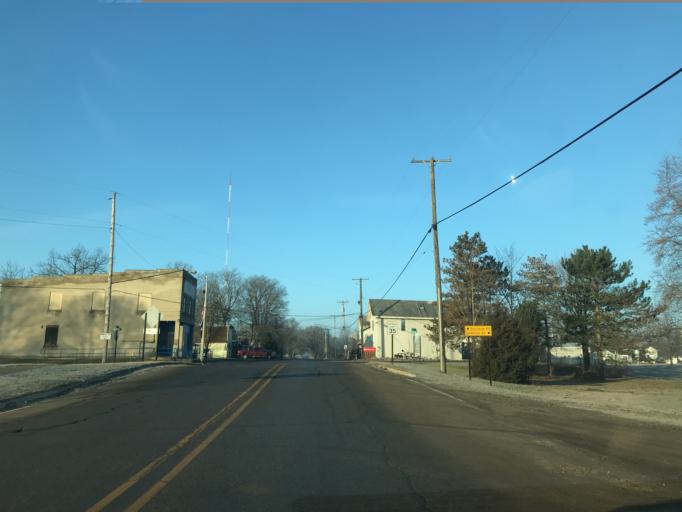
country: US
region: Michigan
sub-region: Eaton County
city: Eaton Rapids
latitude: 42.4439
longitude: -84.5611
